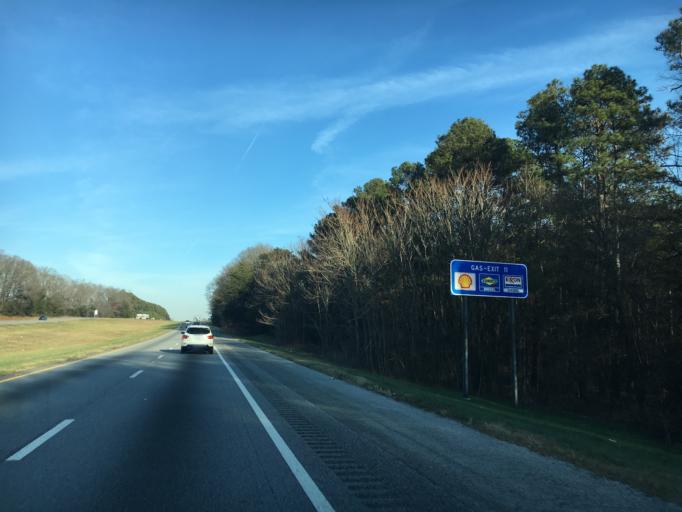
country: US
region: Georgia
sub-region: Hart County
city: Reed Creek
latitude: 34.5230
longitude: -82.8542
